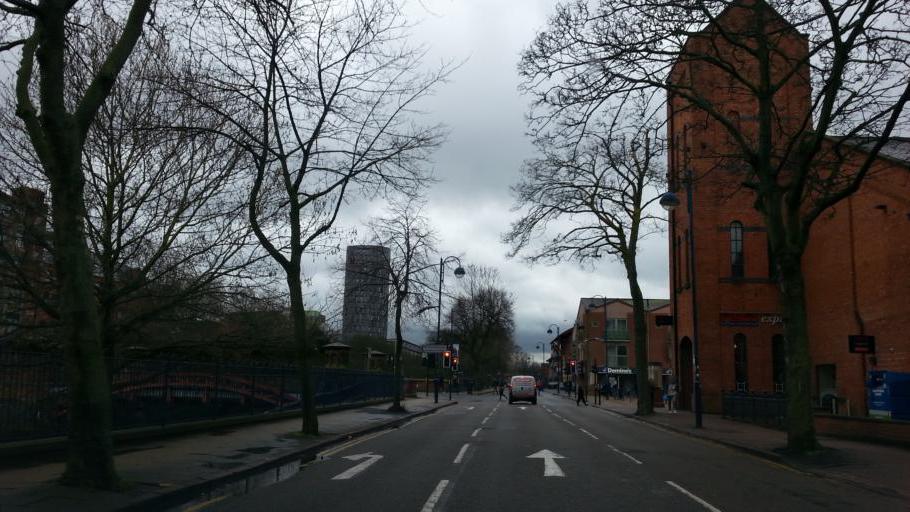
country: GB
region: England
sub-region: City of Leicester
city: Leicester
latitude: 52.6294
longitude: -1.1429
